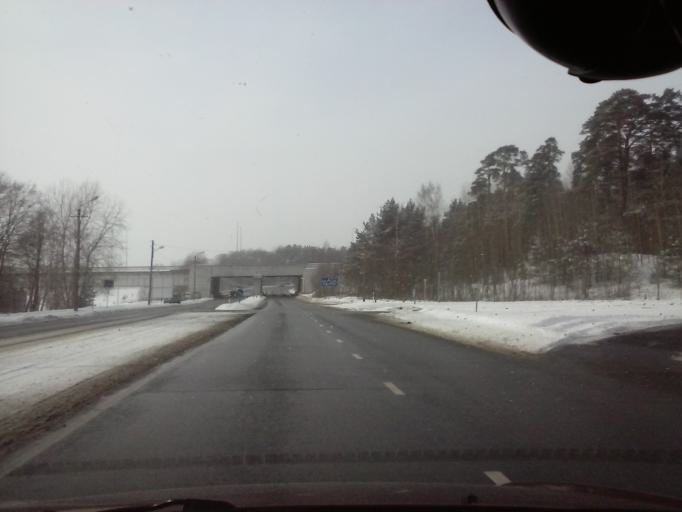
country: EE
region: Paernumaa
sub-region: Paernu linn
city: Parnu
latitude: 58.3788
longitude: 24.5589
